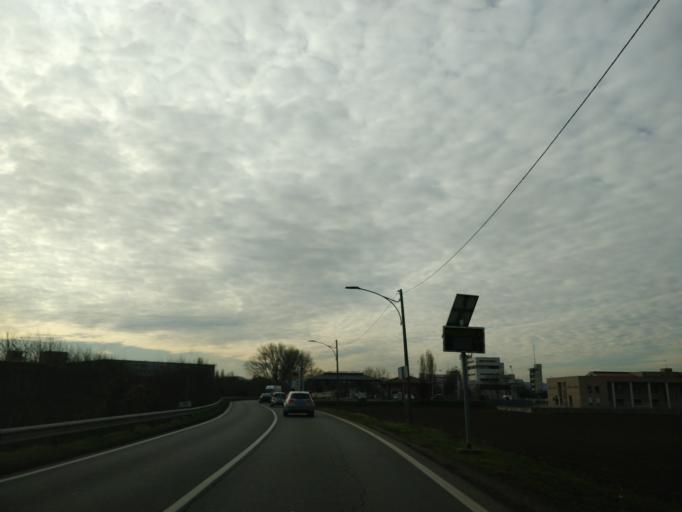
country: IT
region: Emilia-Romagna
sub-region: Provincia di Bologna
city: Progresso
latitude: 44.5384
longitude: 11.3700
